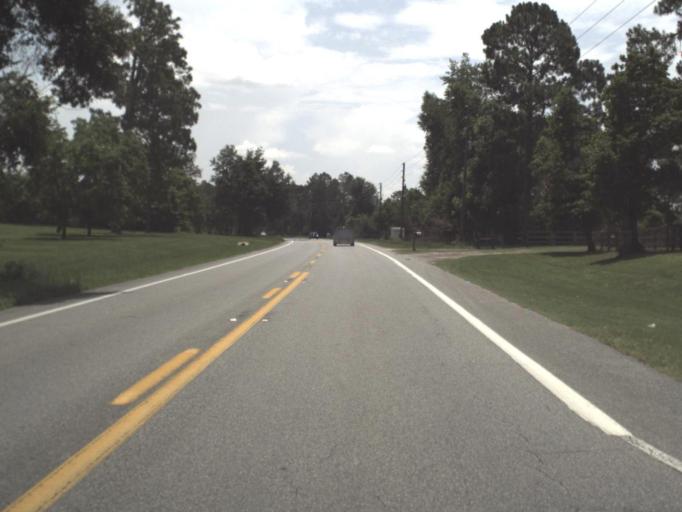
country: US
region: Florida
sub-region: Madison County
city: Madison
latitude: 30.4505
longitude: -83.3470
